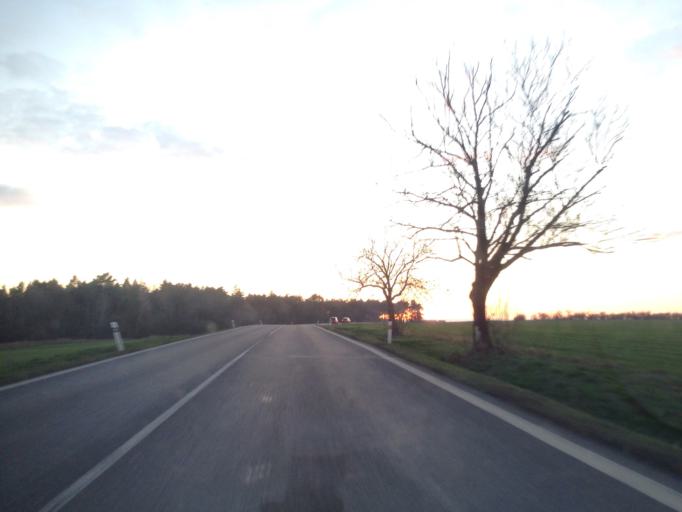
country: CZ
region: Central Bohemia
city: Rakovnik
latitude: 50.1697
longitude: 13.6863
